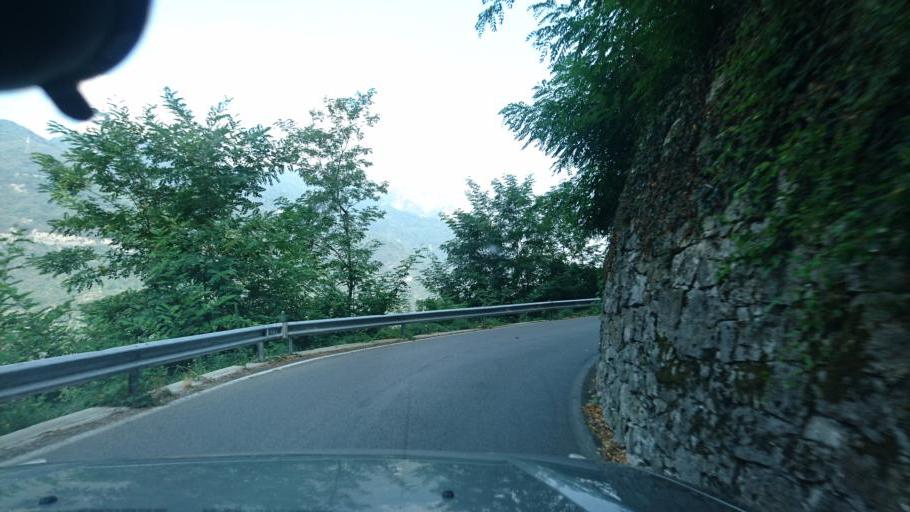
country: IT
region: Lombardy
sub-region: Provincia di Brescia
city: Breno
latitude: 45.9518
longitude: 10.3047
